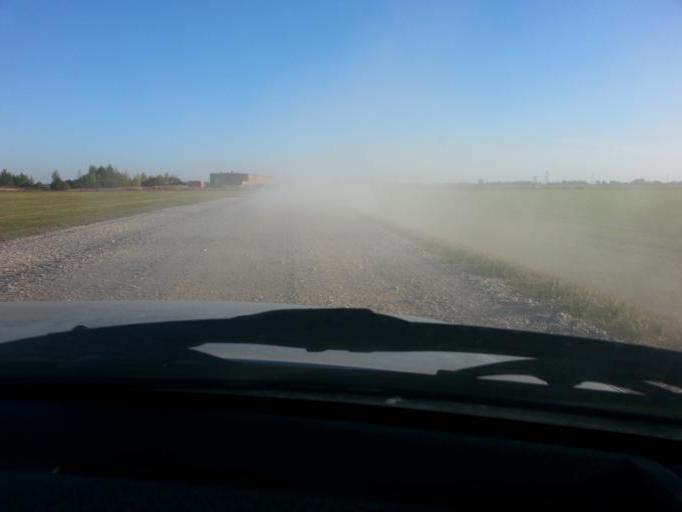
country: LV
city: Tervete
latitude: 56.6156
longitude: 23.4729
